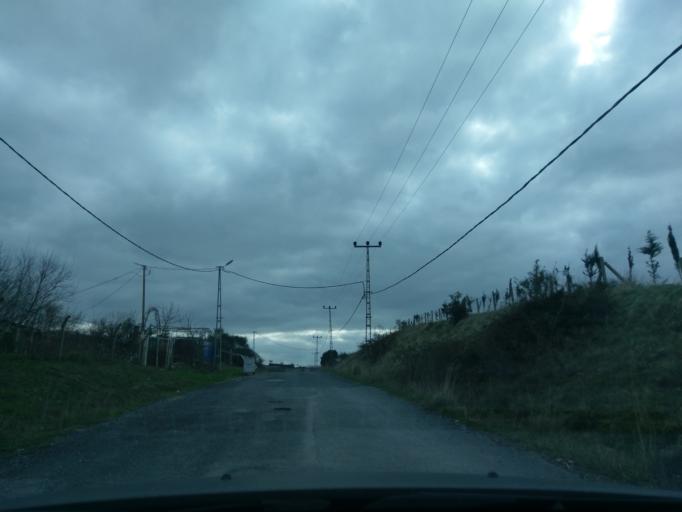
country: TR
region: Istanbul
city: Durusu
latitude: 41.2915
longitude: 28.6846
